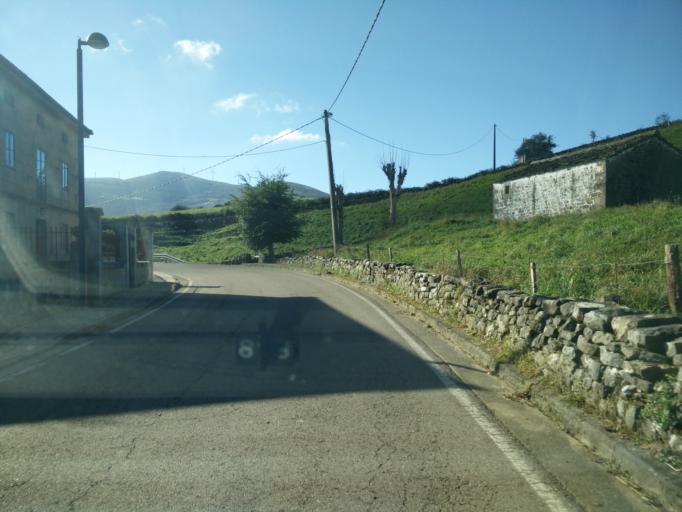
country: ES
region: Cantabria
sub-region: Provincia de Cantabria
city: San Pedro del Romeral
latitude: 43.1108
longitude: -3.8186
